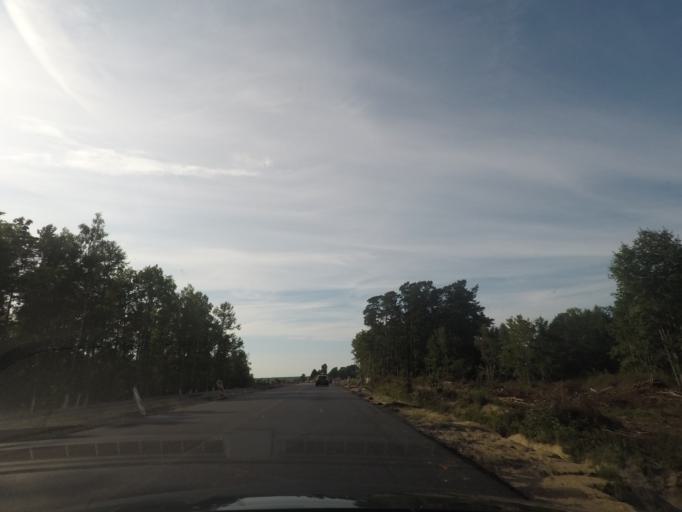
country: PL
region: Pomeranian Voivodeship
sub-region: Powiat leborski
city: Leba
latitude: 54.7333
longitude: 17.5618
